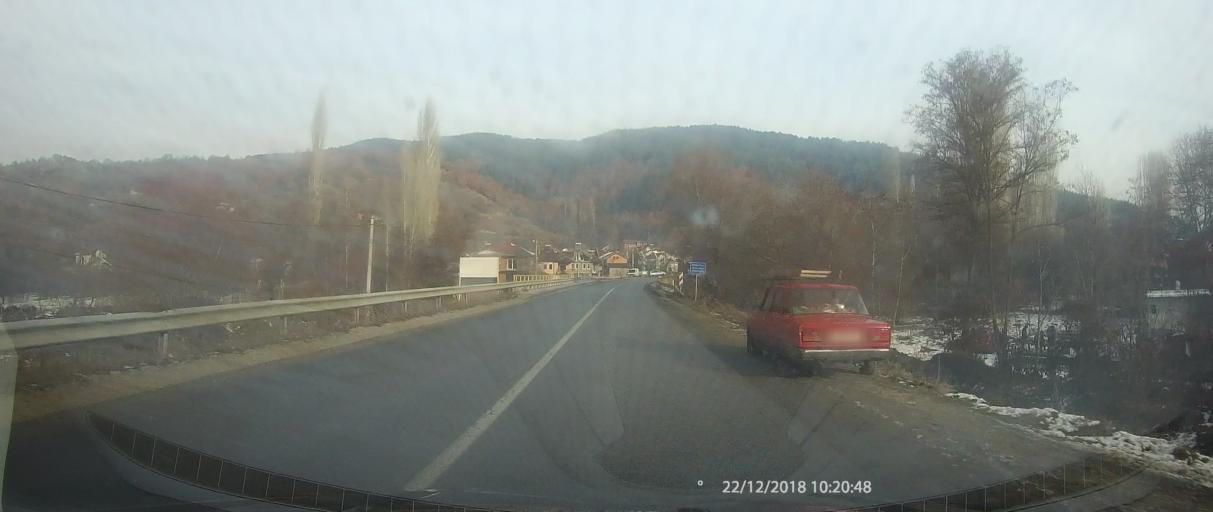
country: MK
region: Kriva Palanka
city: Kriva Palanka
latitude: 42.1937
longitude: 22.3095
